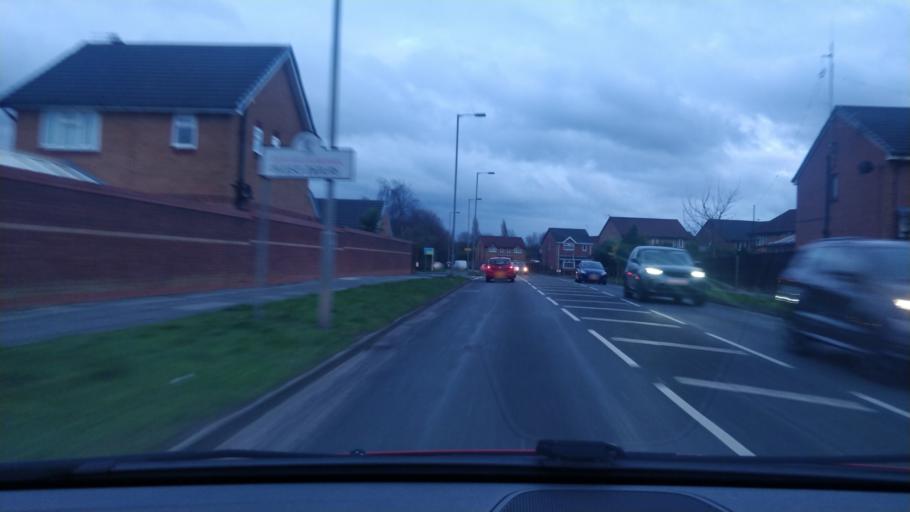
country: GB
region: England
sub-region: Knowsley
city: Kirkby
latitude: 53.4479
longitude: -2.9011
